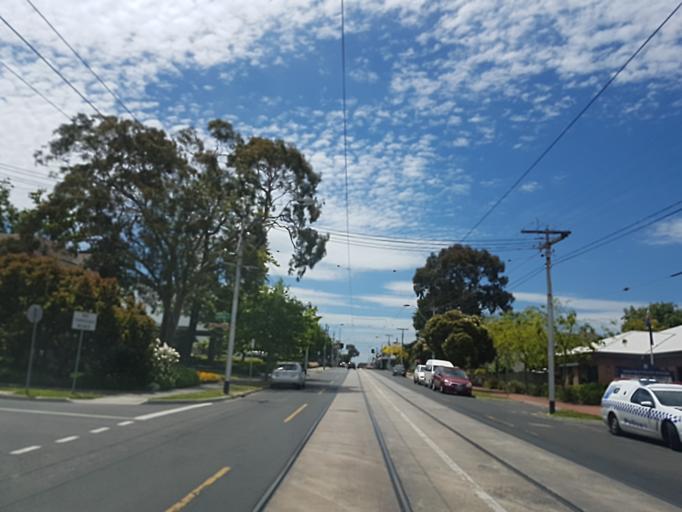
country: AU
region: Victoria
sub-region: Glen Eira
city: Caulfield
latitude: -37.8814
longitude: 145.0230
